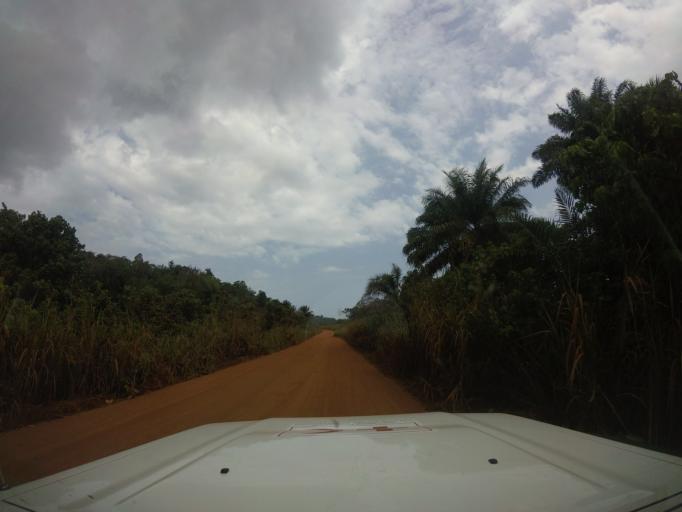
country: LR
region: Grand Cape Mount
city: Robertsport
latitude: 6.7480
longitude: -11.3545
